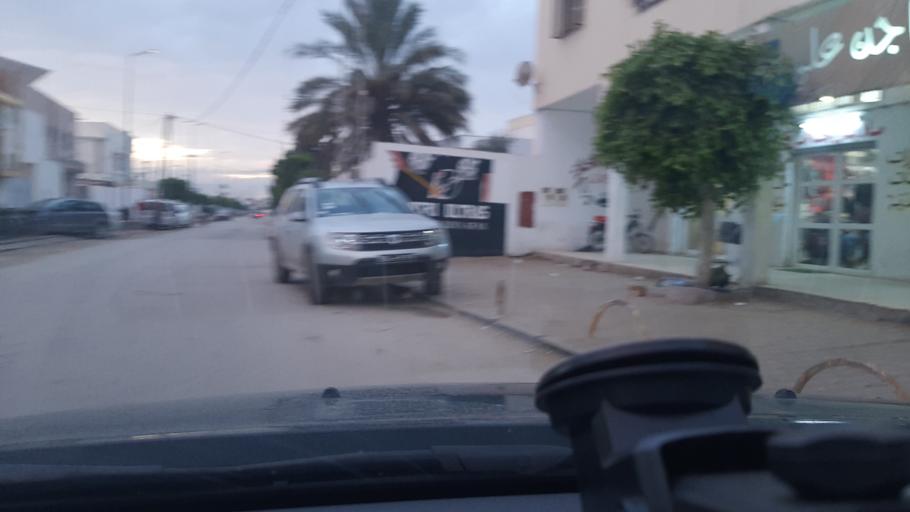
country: TN
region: Safaqis
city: Sfax
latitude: 34.7699
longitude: 10.7059
